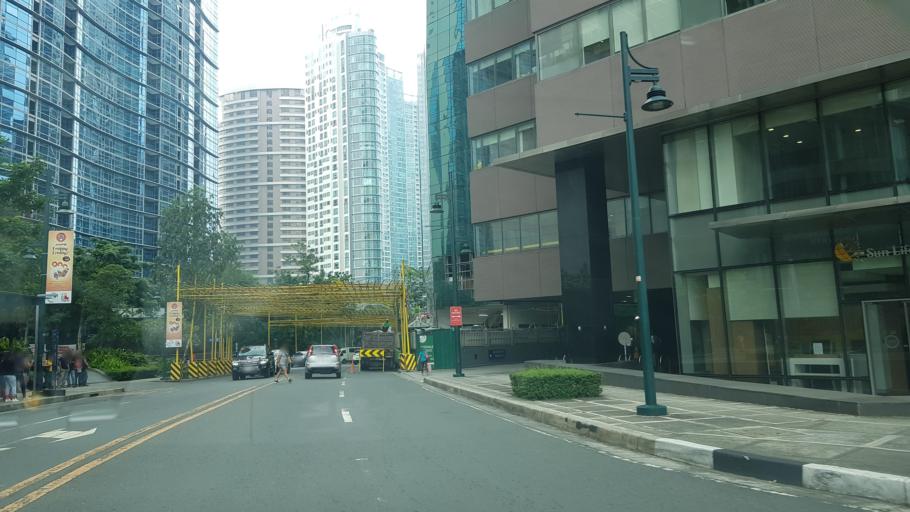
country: PH
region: Metro Manila
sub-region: Makati City
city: Makati City
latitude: 14.5474
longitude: 121.0461
